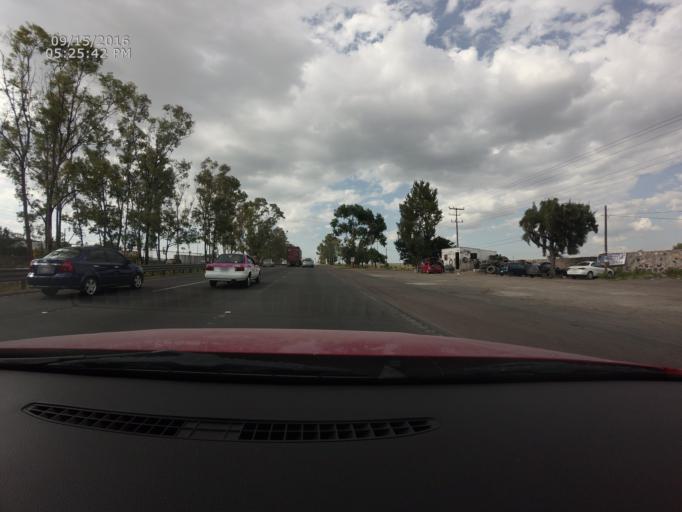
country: MX
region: Mexico
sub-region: Cuautitlan
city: San Jose del Puente
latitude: 19.7314
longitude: -99.2101
